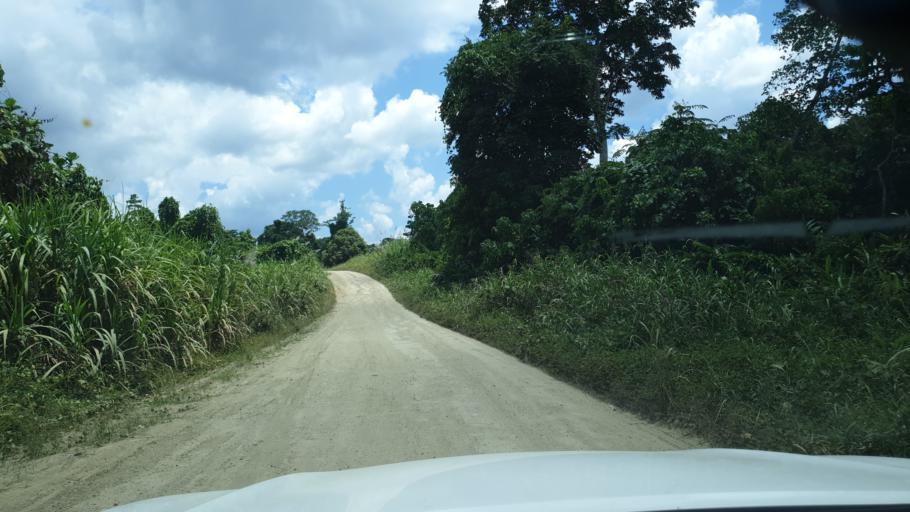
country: PG
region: East Sepik
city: Angoram
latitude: -3.8998
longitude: 143.9274
